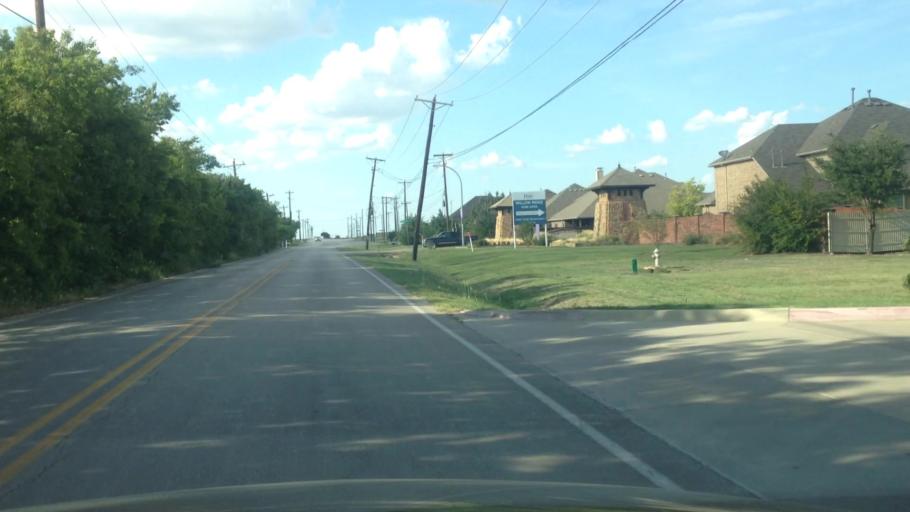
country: US
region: Texas
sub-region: Tarrant County
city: Haslet
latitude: 32.9367
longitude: -97.3920
